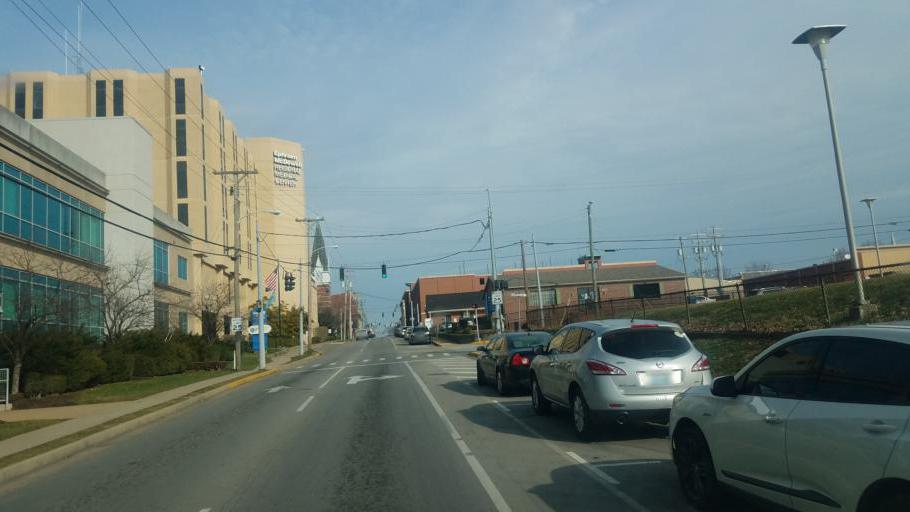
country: US
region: Kentucky
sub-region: Boyle County
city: Danville
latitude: 37.6431
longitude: -84.7728
